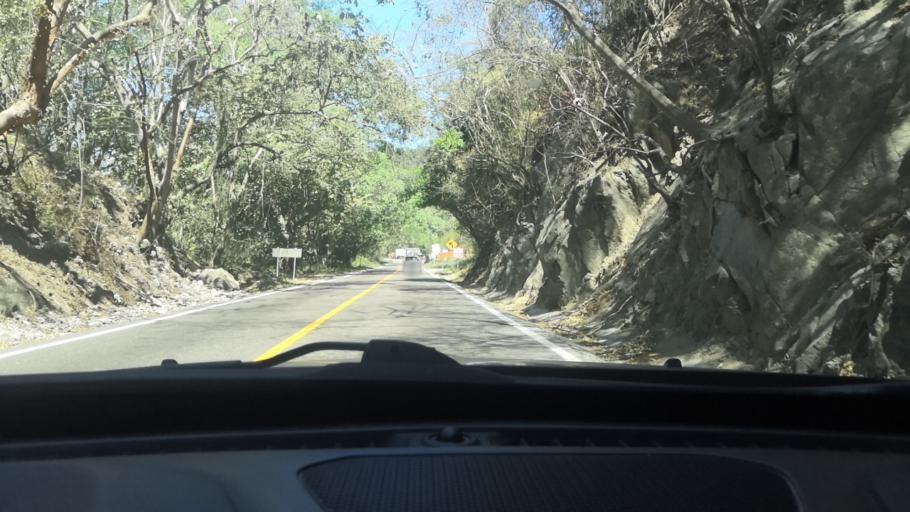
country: MX
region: Nayarit
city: Bucerias
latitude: 20.8189
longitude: -105.3899
